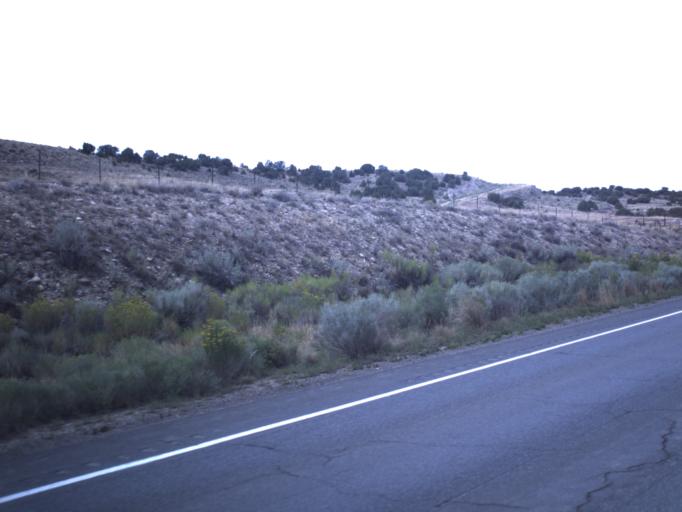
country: US
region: Utah
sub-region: Duchesne County
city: Duchesne
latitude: 40.1663
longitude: -110.2906
